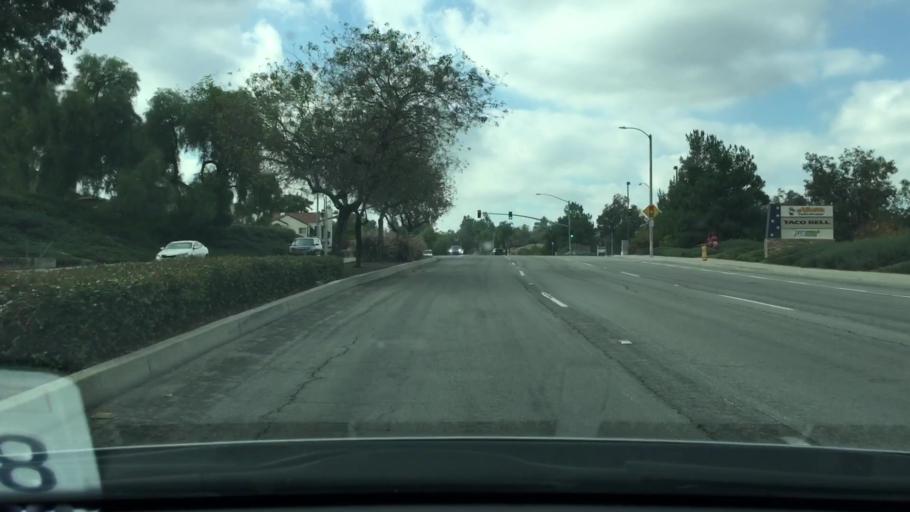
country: US
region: California
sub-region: San Bernardino County
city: Chino Hills
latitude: 34.0107
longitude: -117.7380
